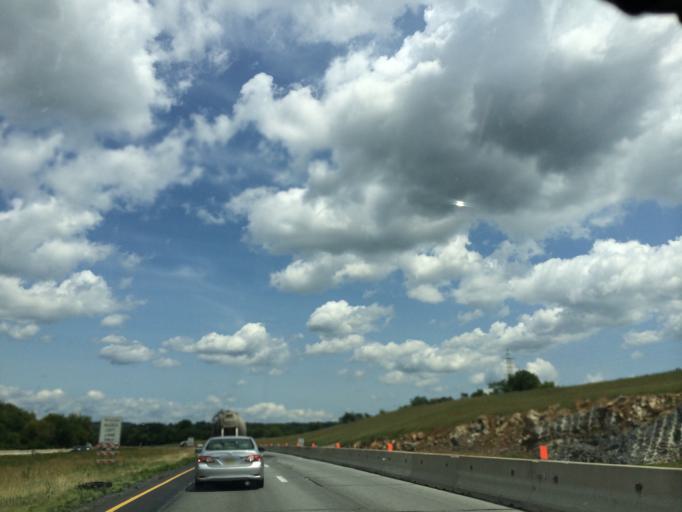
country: US
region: Pennsylvania
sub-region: Northampton County
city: Tatamy
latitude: 40.7416
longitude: -75.2658
